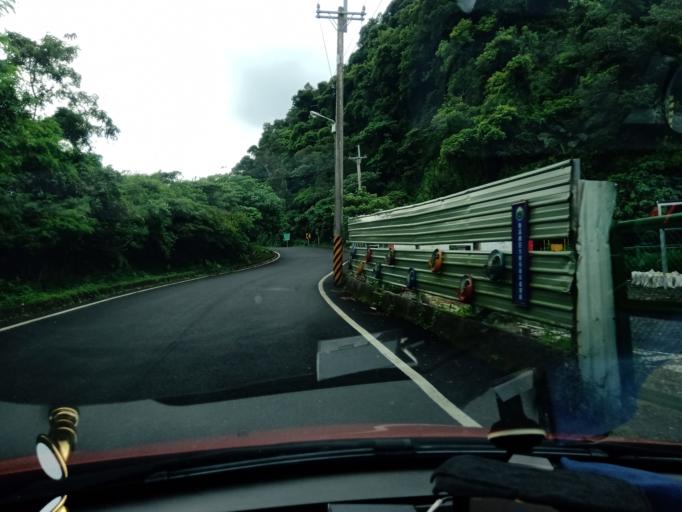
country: TW
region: Taiwan
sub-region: Yilan
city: Yilan
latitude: 24.7818
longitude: 121.7065
